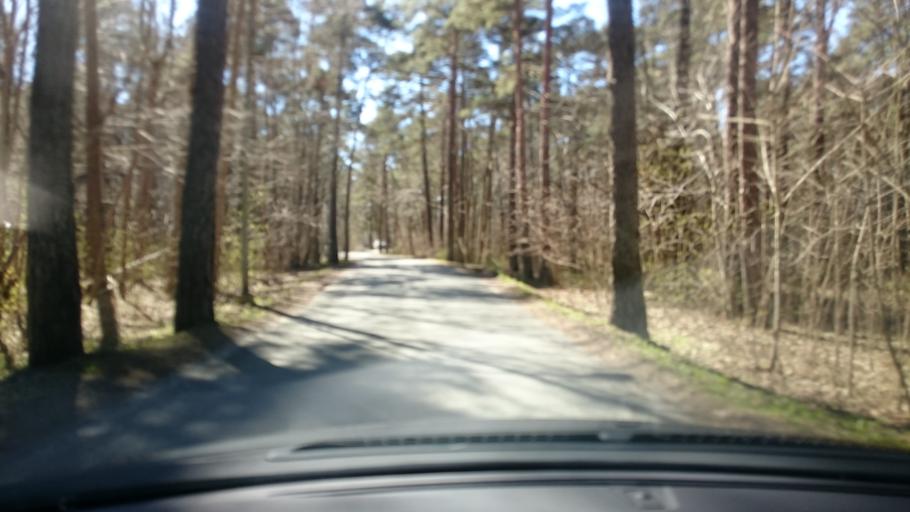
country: EE
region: Harju
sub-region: Tallinna linn
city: Kose
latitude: 59.4589
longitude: 24.8444
